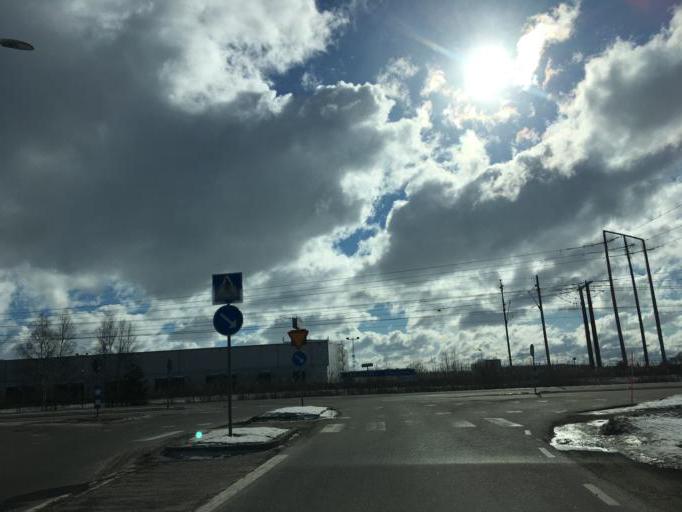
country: SE
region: Vaestmanland
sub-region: Vasteras
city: Vasteras
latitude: 59.5911
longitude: 16.4700
